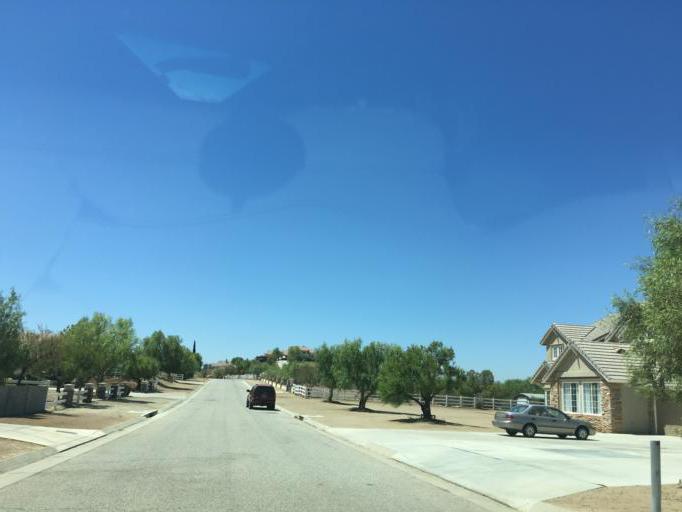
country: US
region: California
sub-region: Los Angeles County
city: Agua Dulce
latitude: 34.5140
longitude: -118.3035
